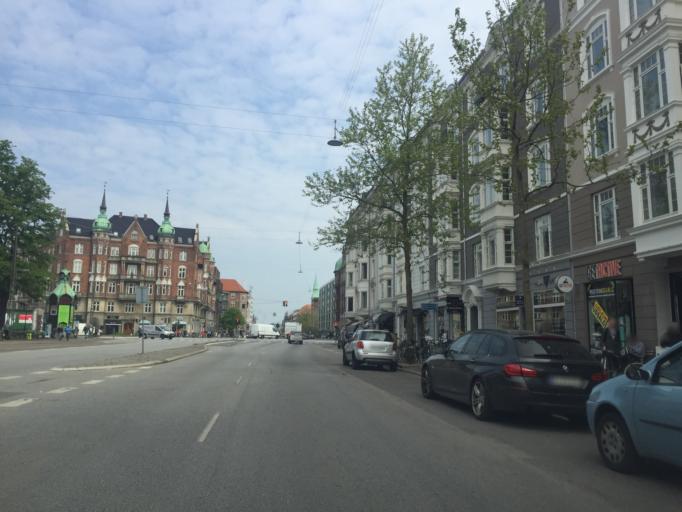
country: DK
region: Capital Region
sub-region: Kobenhavn
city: Copenhagen
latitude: 55.7082
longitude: 12.5775
